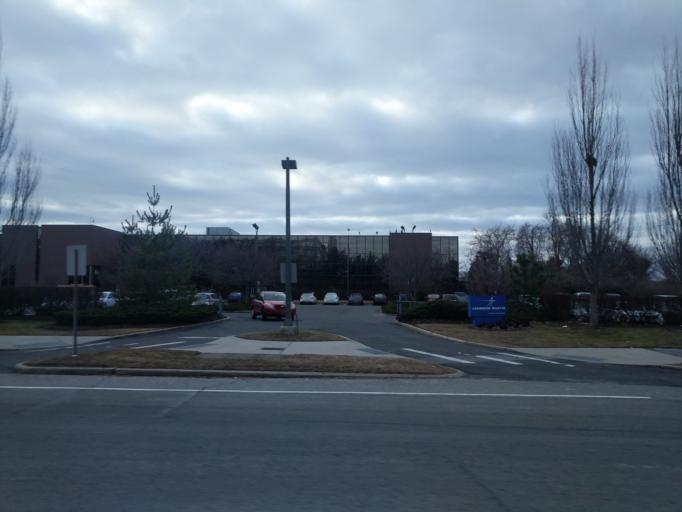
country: US
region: New York
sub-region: Nassau County
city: East Garden City
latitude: 40.7229
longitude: -73.6036
